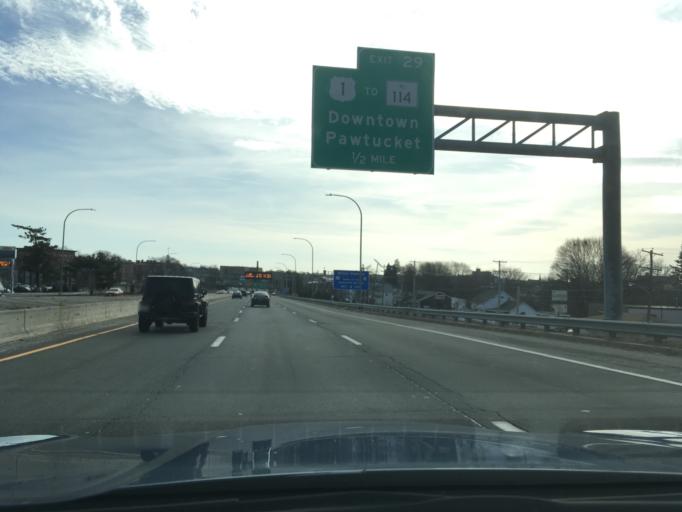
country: US
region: Rhode Island
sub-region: Providence County
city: Pawtucket
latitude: 41.8902
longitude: -71.3791
